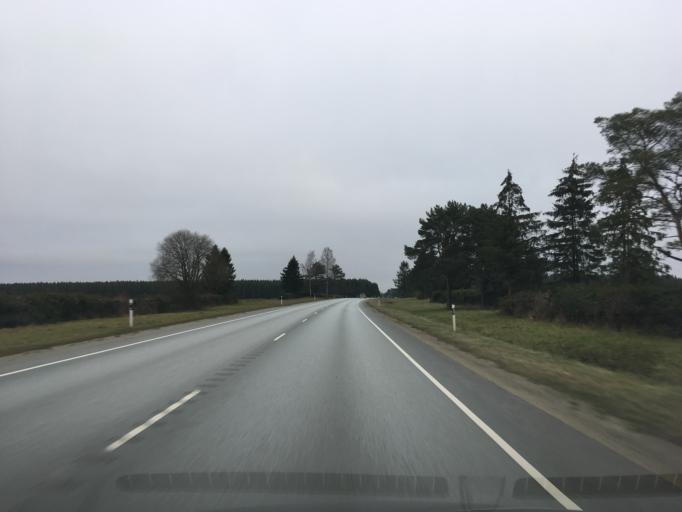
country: EE
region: Laeaene-Virumaa
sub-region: Viru-Nigula vald
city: Kunda
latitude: 59.3891
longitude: 26.6171
